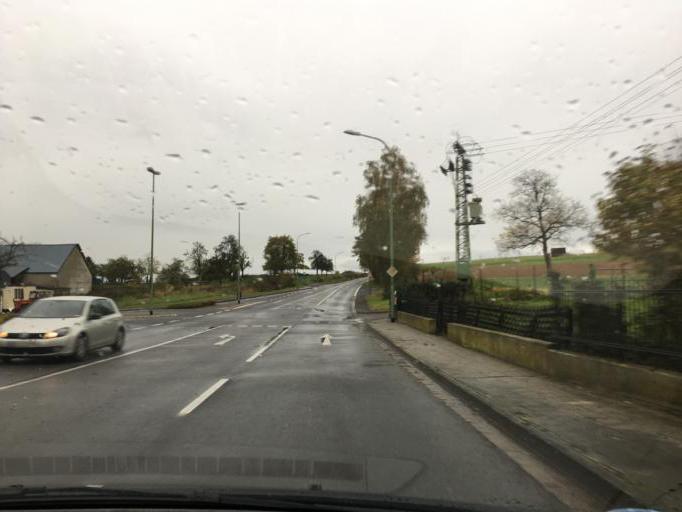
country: DE
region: North Rhine-Westphalia
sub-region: Regierungsbezirk Koln
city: Vettweiss
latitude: 50.7122
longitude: 6.5709
